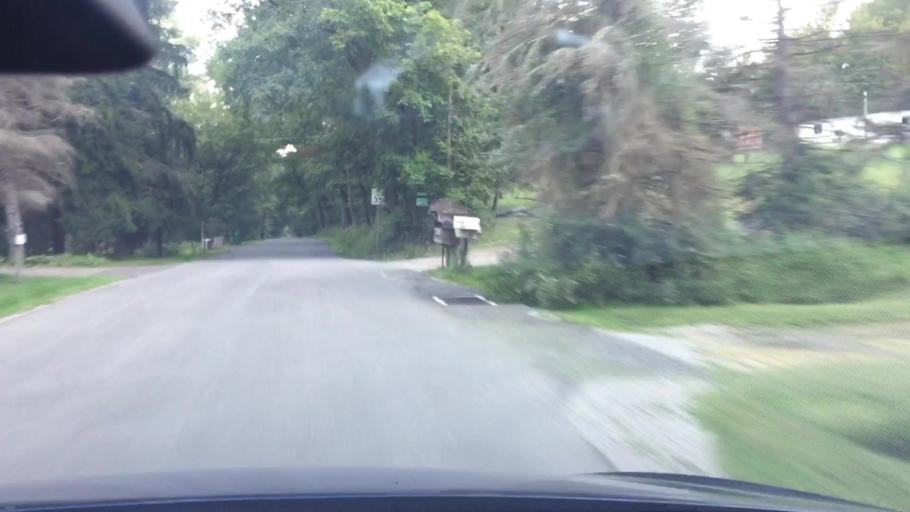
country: US
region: Pennsylvania
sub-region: Butler County
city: Oak Hills
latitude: 40.7973
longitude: -79.8869
